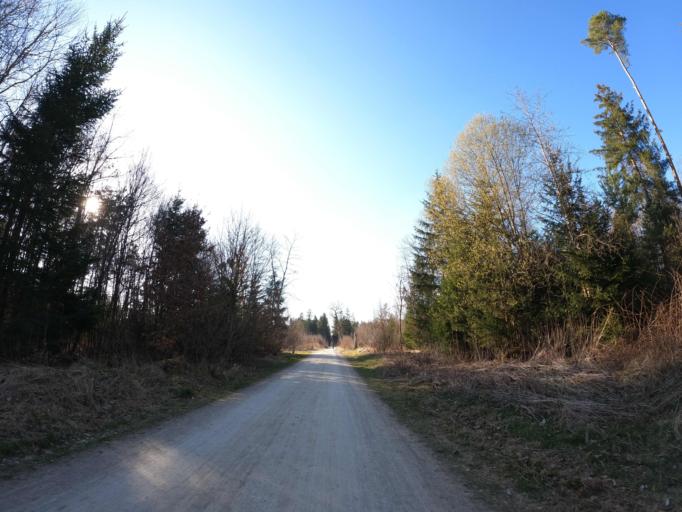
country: DE
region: Bavaria
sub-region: Upper Bavaria
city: Unterhaching
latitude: 48.0703
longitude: 11.5891
